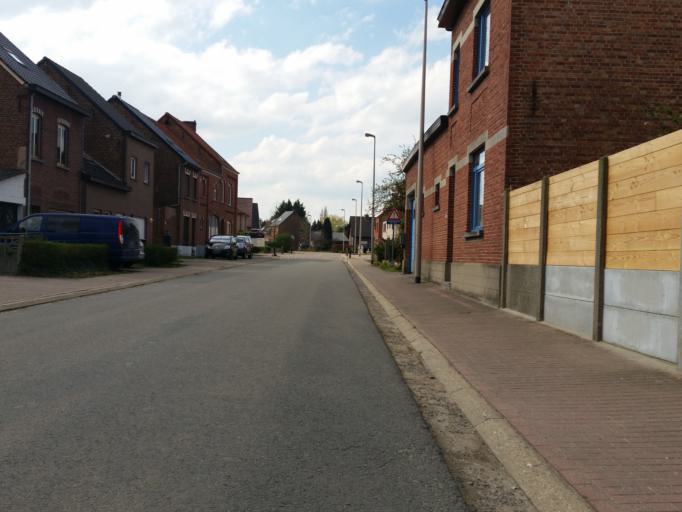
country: BE
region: Flanders
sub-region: Provincie Vlaams-Brabant
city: Kampenhout
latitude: 50.9300
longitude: 4.5474
